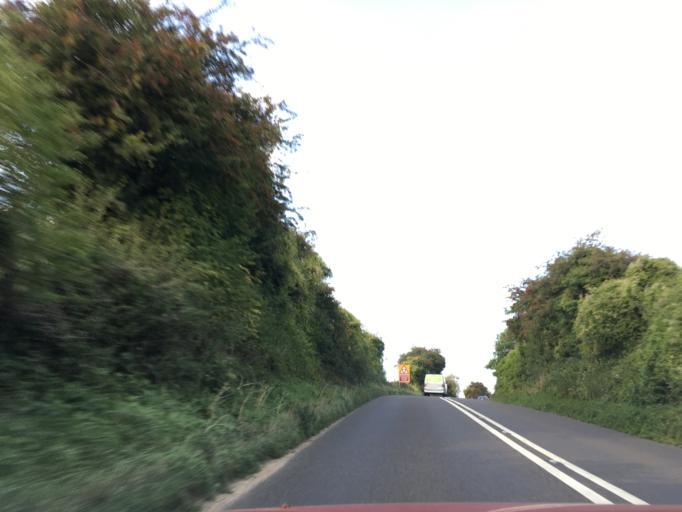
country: GB
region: England
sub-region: Gloucestershire
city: Northleach
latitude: 51.8348
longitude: -1.8400
